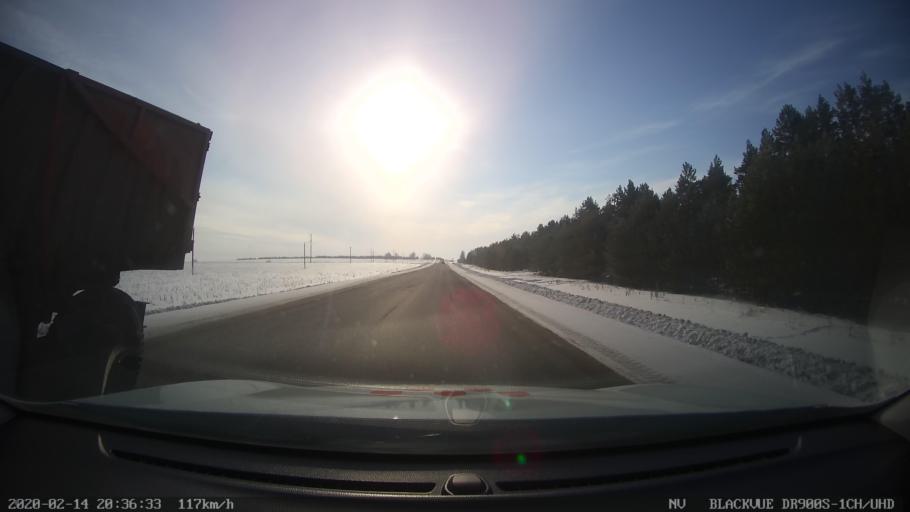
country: RU
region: Tatarstan
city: Kuybyshevskiy Zaton
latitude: 55.3653
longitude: 49.0007
